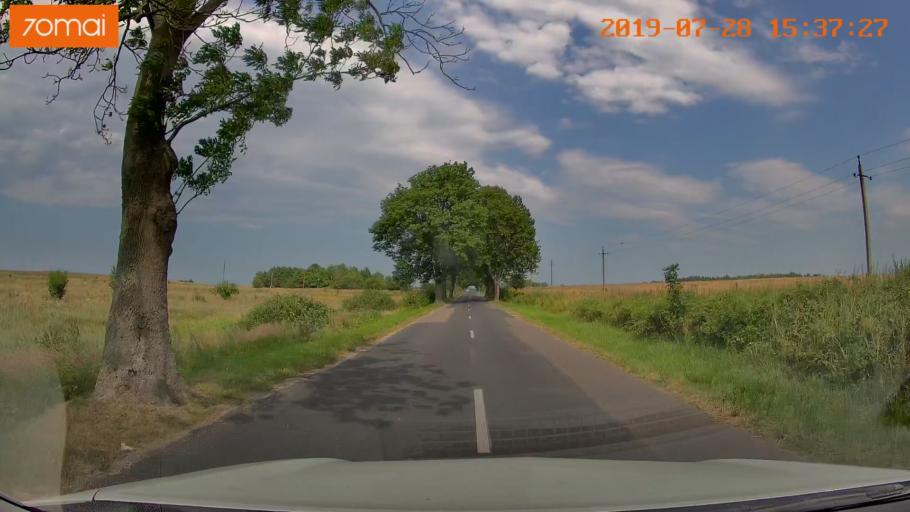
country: RU
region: Kaliningrad
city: Donskoye
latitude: 54.8919
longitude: 19.9999
